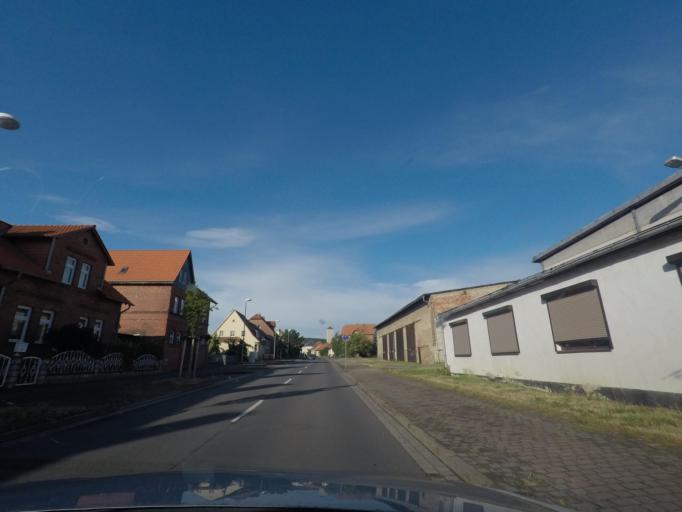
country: DE
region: Saxony-Anhalt
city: Huy-Neinstedt
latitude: 51.9881
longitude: 10.8911
